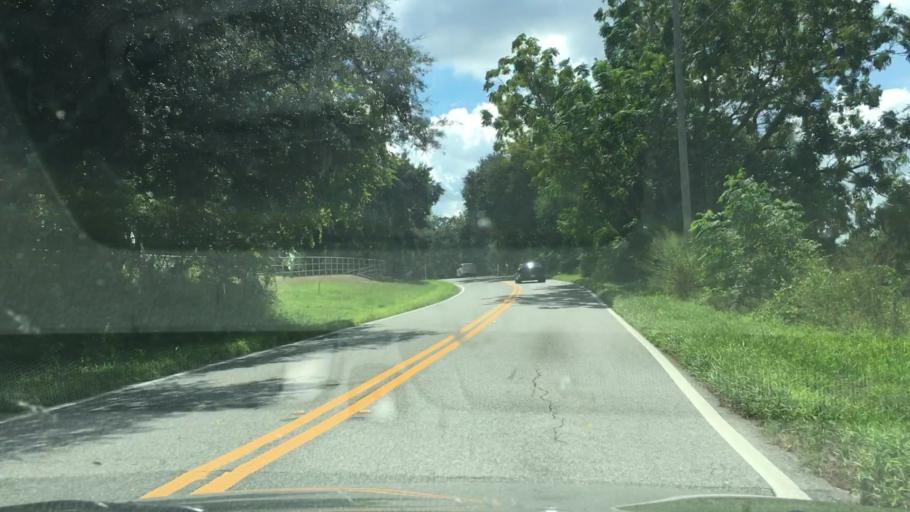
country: US
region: Florida
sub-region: Lake County
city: Montverde
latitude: 28.5669
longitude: -81.7021
